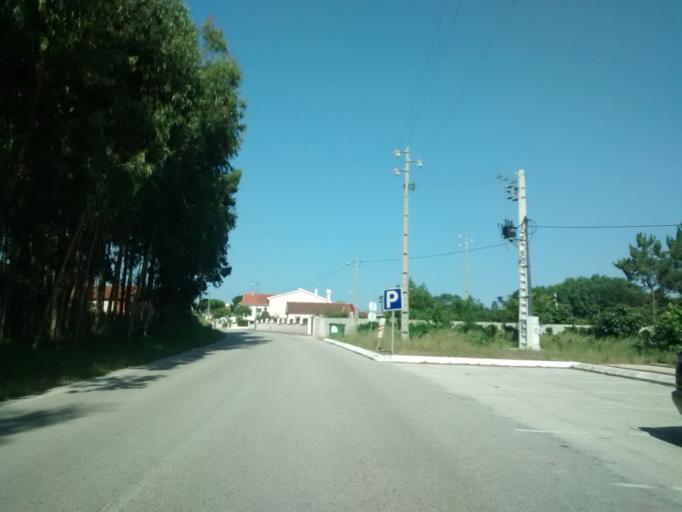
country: PT
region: Leiria
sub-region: Pombal
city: Lourical
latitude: 39.9798
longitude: -8.8132
